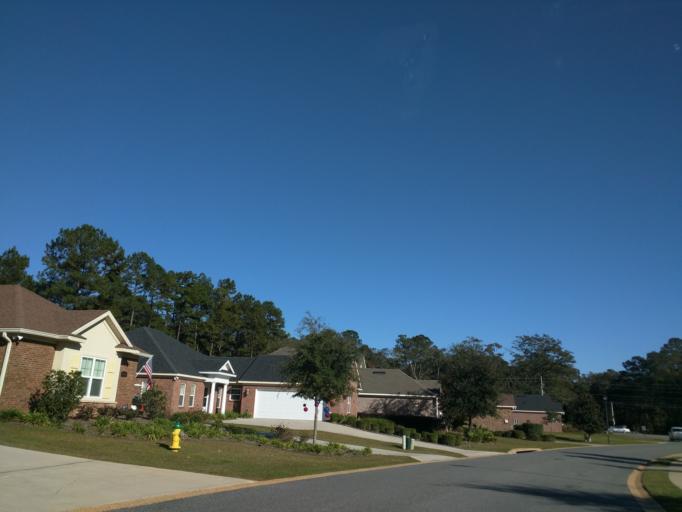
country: US
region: Florida
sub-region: Leon County
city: Tallahassee
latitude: 30.4770
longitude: -84.2118
